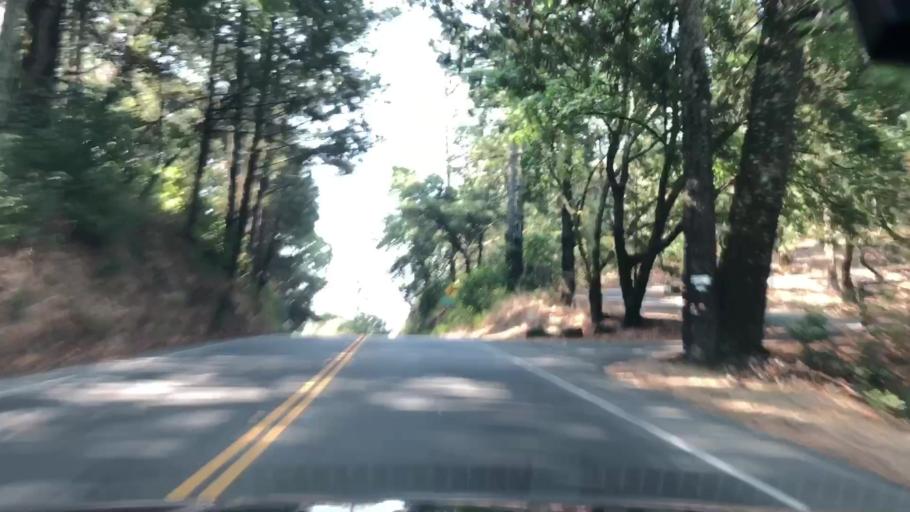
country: US
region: California
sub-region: Napa County
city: Calistoga
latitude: 38.5709
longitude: -122.6263
